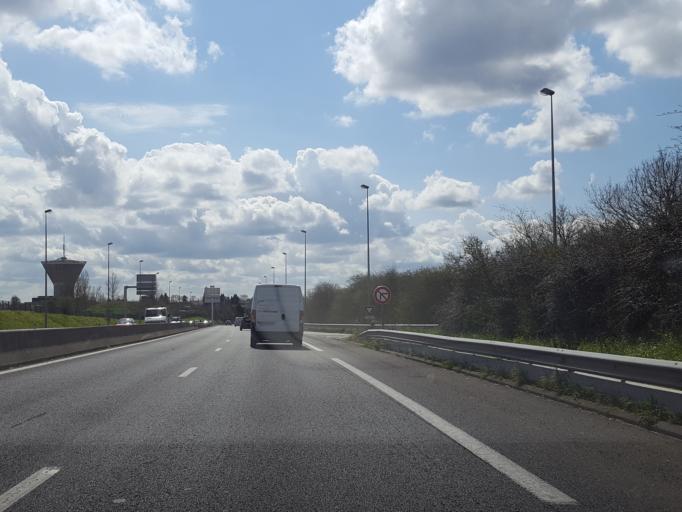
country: FR
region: Centre
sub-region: Departement du Loiret
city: Saint-Jean-de-la-Ruelle
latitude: 47.9261
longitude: 1.8747
